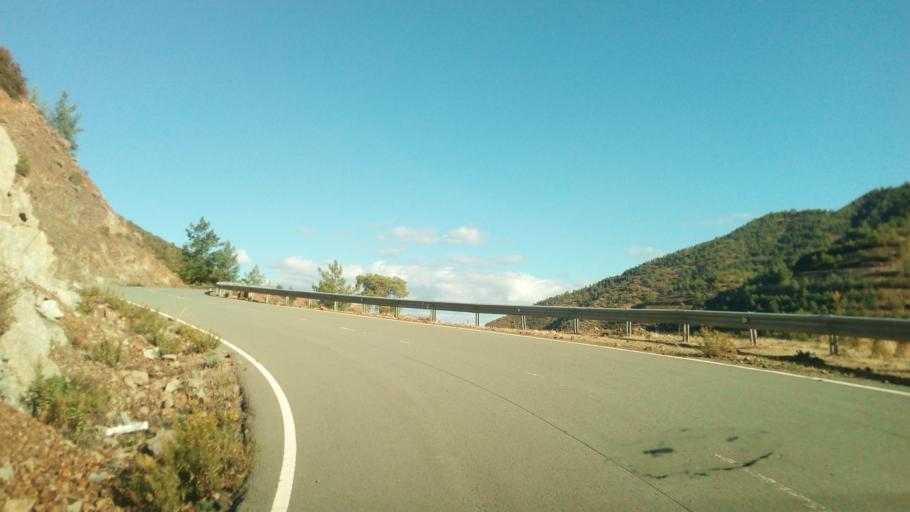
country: CY
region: Lefkosia
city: Lefka
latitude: 35.0910
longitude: 32.7586
